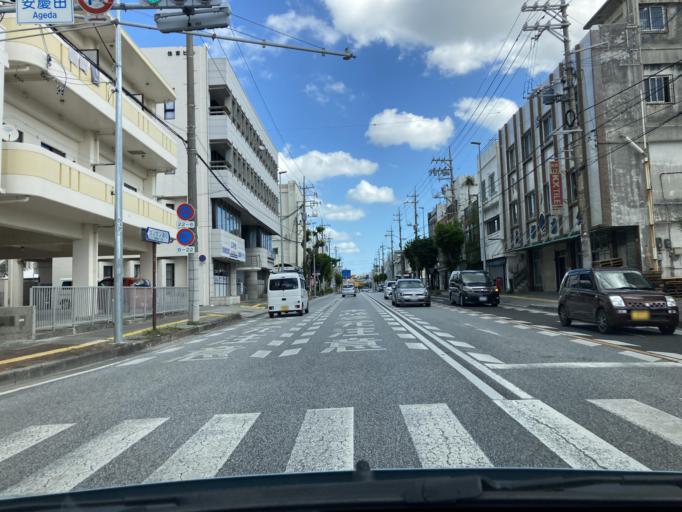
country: JP
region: Okinawa
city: Okinawa
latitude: 26.3381
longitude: 127.8106
